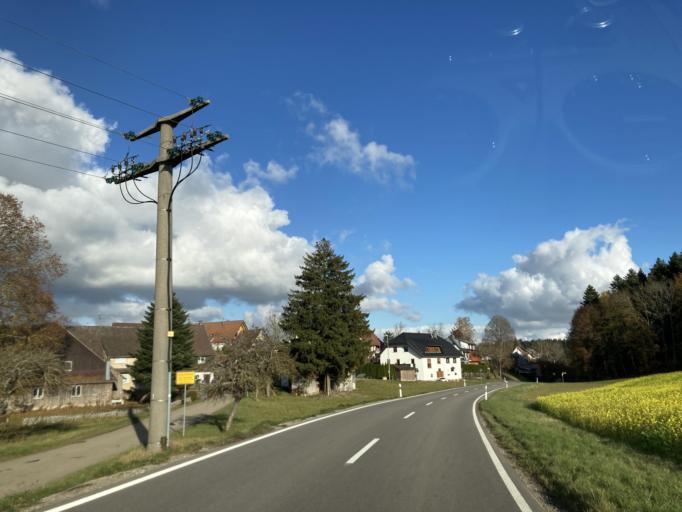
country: DE
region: Baden-Wuerttemberg
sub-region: Freiburg Region
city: Dornhan
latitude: 48.3442
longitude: 8.4828
